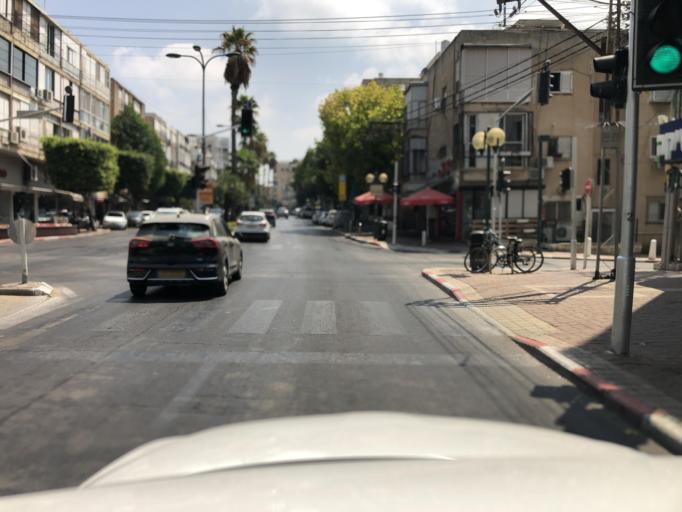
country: IL
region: Tel Aviv
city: Giv`atayim
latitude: 32.0751
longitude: 34.8061
